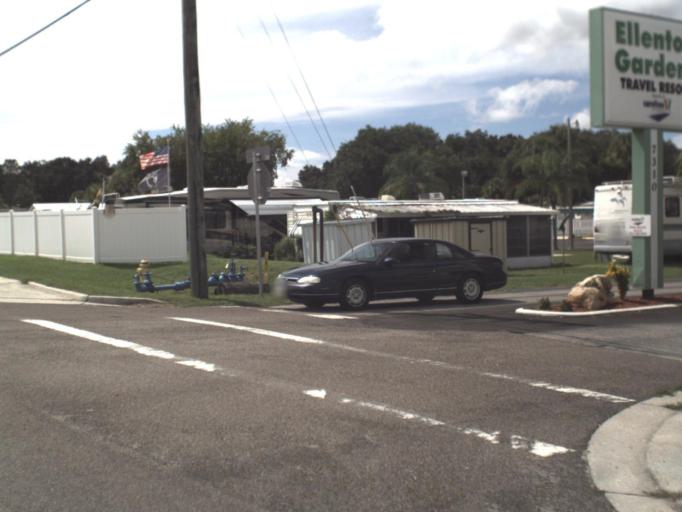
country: US
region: Florida
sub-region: Manatee County
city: Ellenton
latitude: 27.5373
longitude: -82.4882
